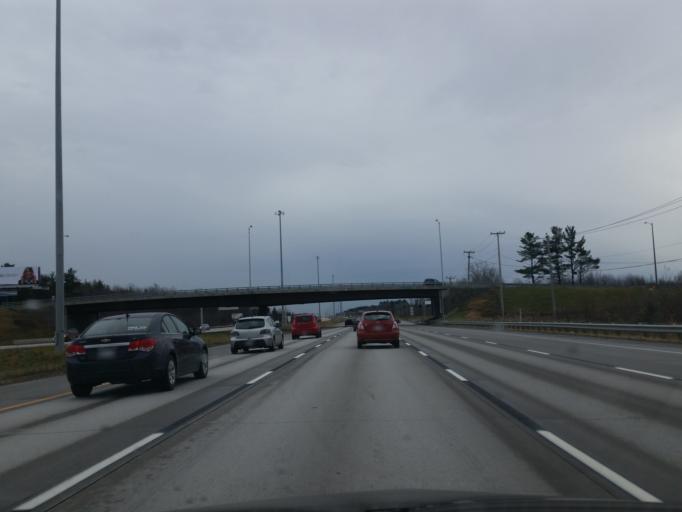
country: CA
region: Quebec
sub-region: Laurentides
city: Blainville
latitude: 45.6771
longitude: -73.9141
